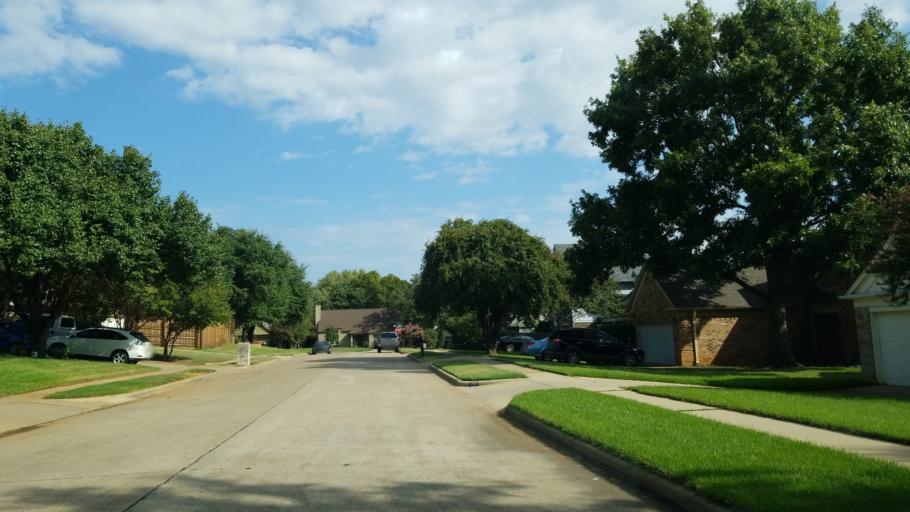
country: US
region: Texas
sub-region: Tarrant County
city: Grapevine
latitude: 32.8891
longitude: -97.0847
